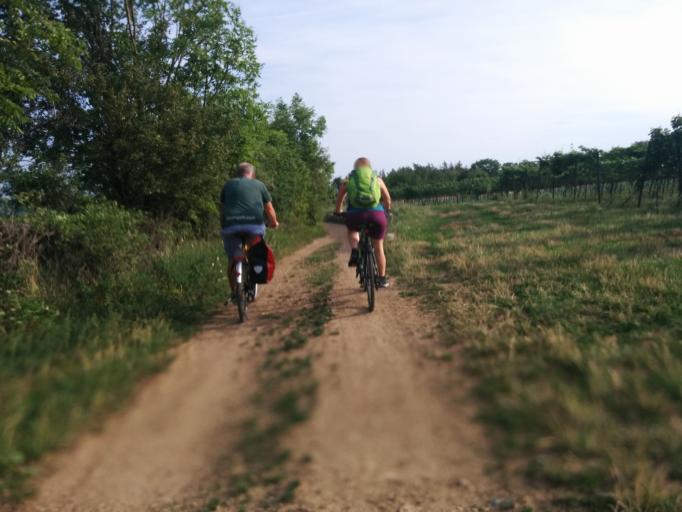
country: AT
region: Lower Austria
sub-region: Politischer Bezirk Modling
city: Gumpoldskirchen
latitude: 48.0489
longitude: 16.2664
